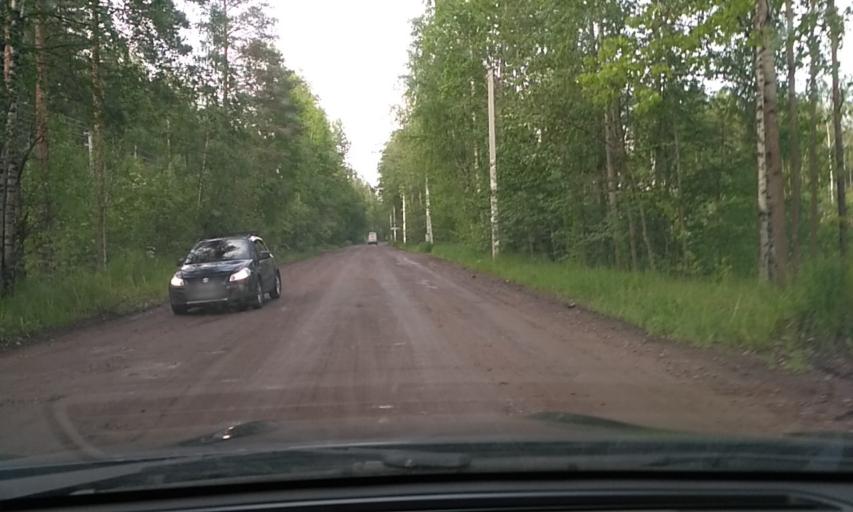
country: RU
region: Leningrad
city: Otradnoye
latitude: 59.7858
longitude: 30.7753
